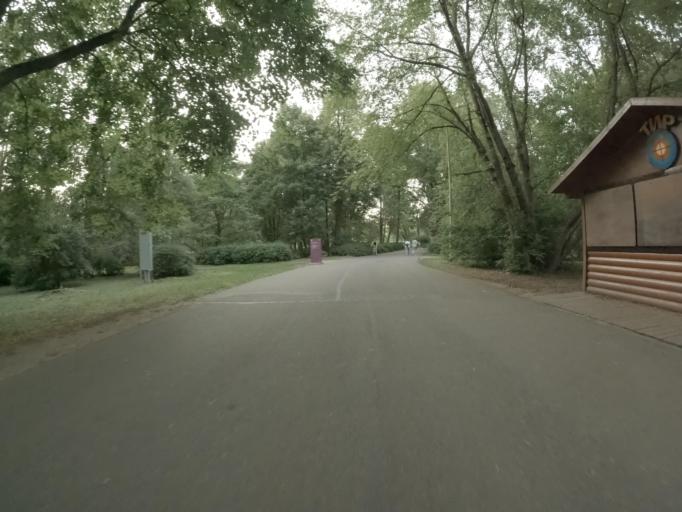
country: RU
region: Leningrad
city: Krestovskiy ostrov
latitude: 59.9797
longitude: 30.2538
